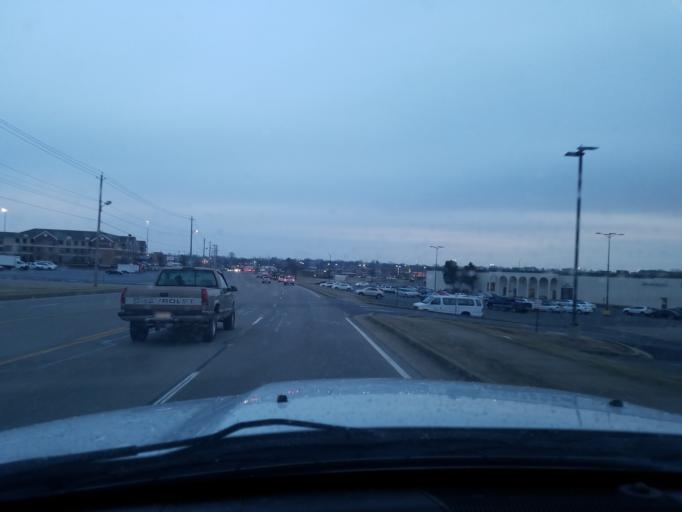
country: US
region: Kentucky
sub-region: Warren County
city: Bowling Green
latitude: 36.9639
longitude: -86.4719
